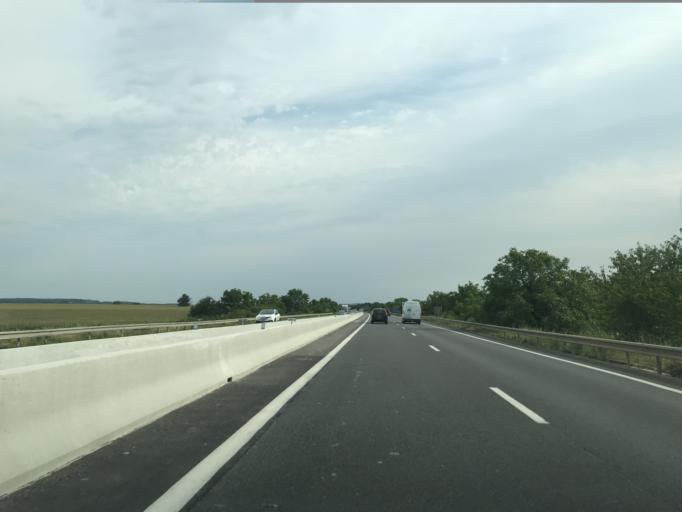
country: FR
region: Centre
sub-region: Departement d'Indre-et-Loire
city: Sainte-Maure-de-Touraine
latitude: 47.1009
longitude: 0.5886
